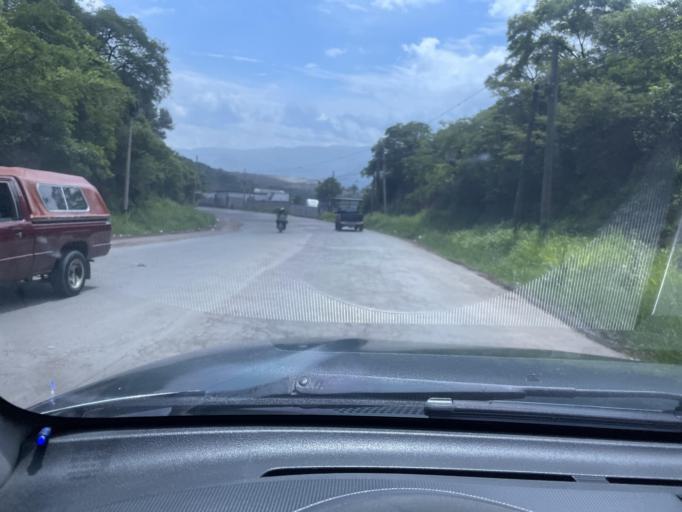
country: HN
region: Francisco Morazan
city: Rio Abajo
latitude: 14.1394
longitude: -87.2309
